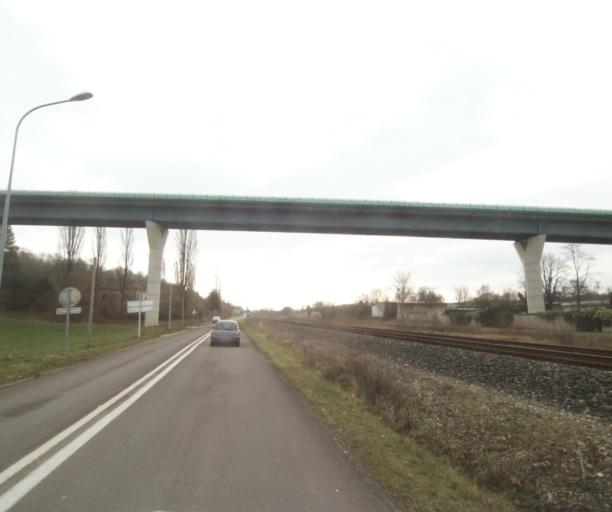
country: FR
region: Lorraine
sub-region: Departement de la Meuse
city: Ancerville
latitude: 48.6272
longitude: 4.9944
